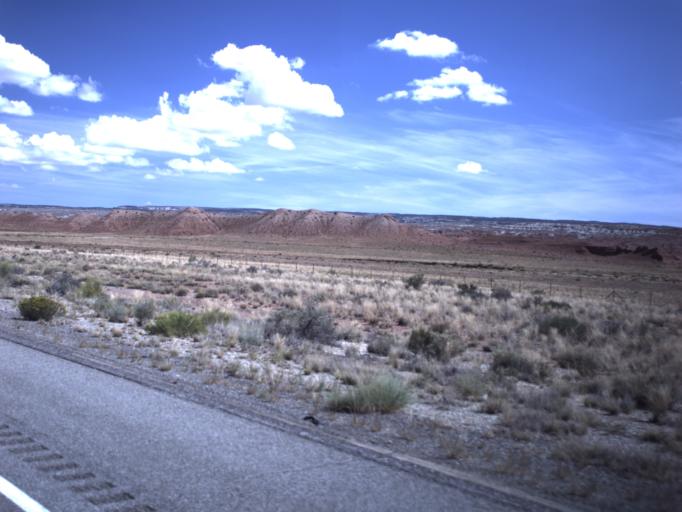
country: US
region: Utah
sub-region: Emery County
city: Ferron
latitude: 38.8395
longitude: -111.0704
